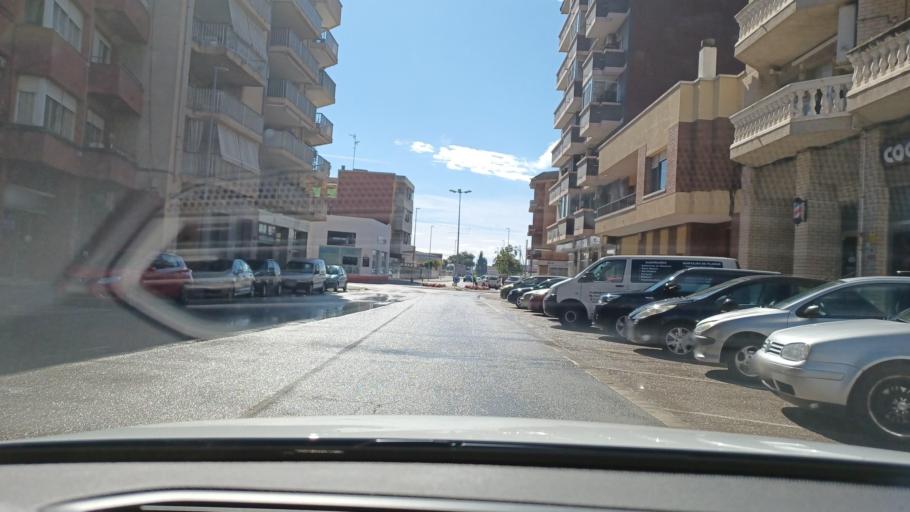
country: ES
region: Catalonia
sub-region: Provincia de Tarragona
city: Amposta
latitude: 40.7028
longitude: 0.5793
